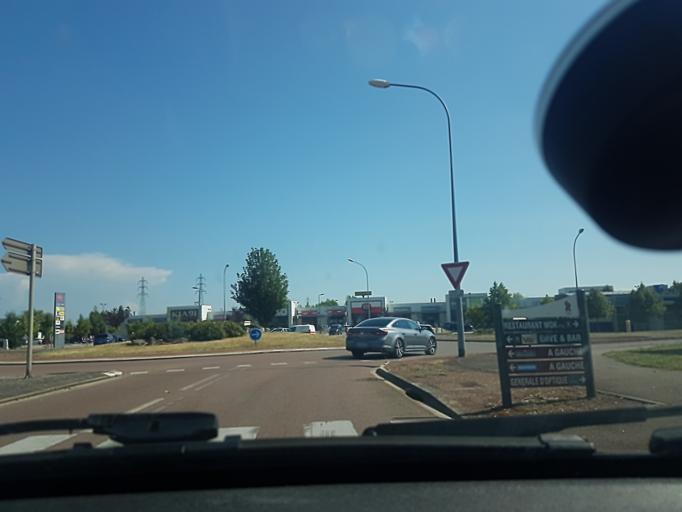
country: FR
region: Bourgogne
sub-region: Departement de Saone-et-Loire
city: Chalon-sur-Saone
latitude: 46.7729
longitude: 4.8653
